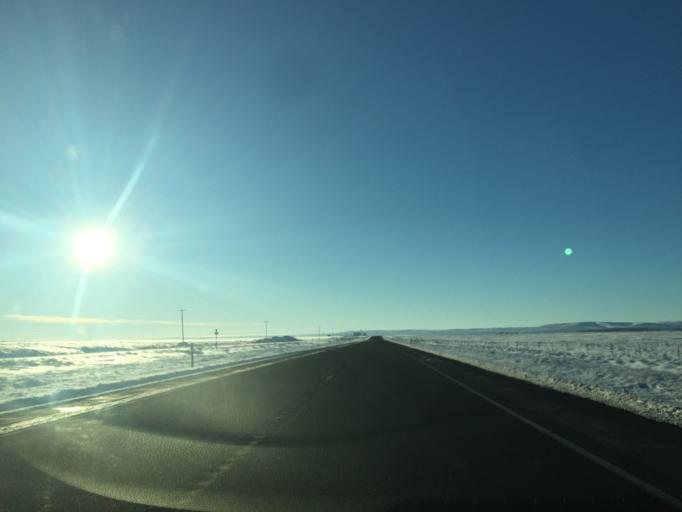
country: US
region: Washington
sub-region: Okanogan County
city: Coulee Dam
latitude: 47.6612
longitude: -119.2100
